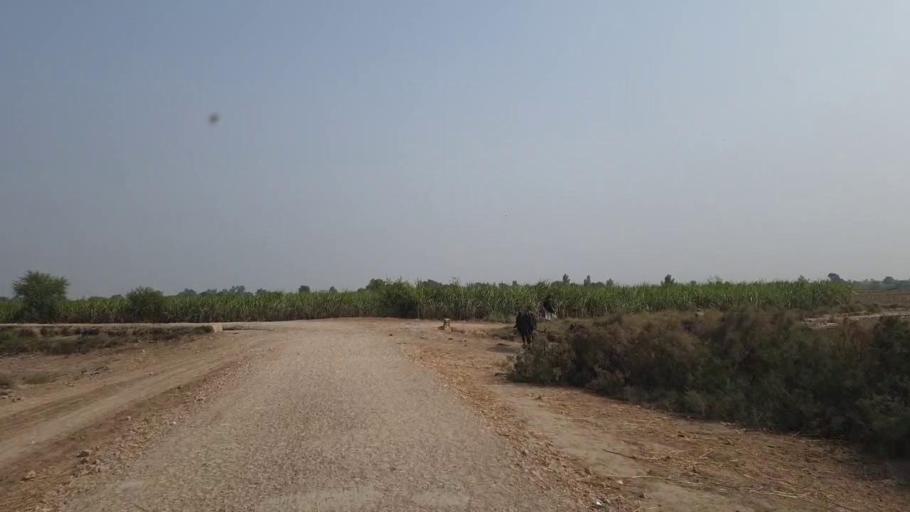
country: PK
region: Sindh
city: Kario
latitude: 24.9081
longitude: 68.5980
